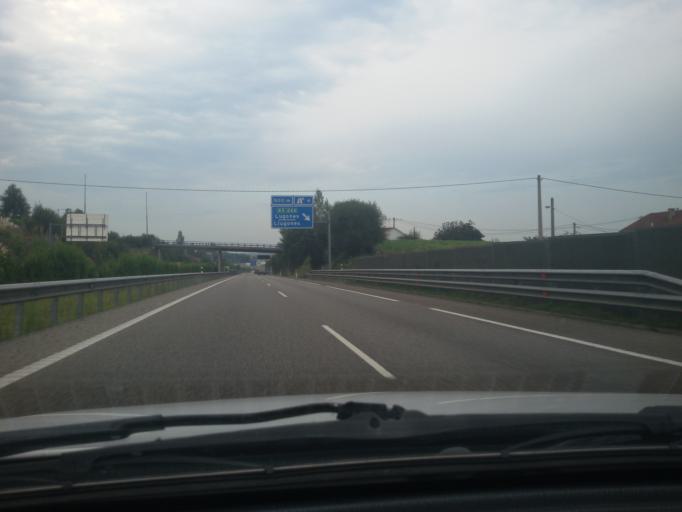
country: ES
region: Asturias
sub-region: Province of Asturias
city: Lugones
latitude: 43.3919
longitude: -5.8261
